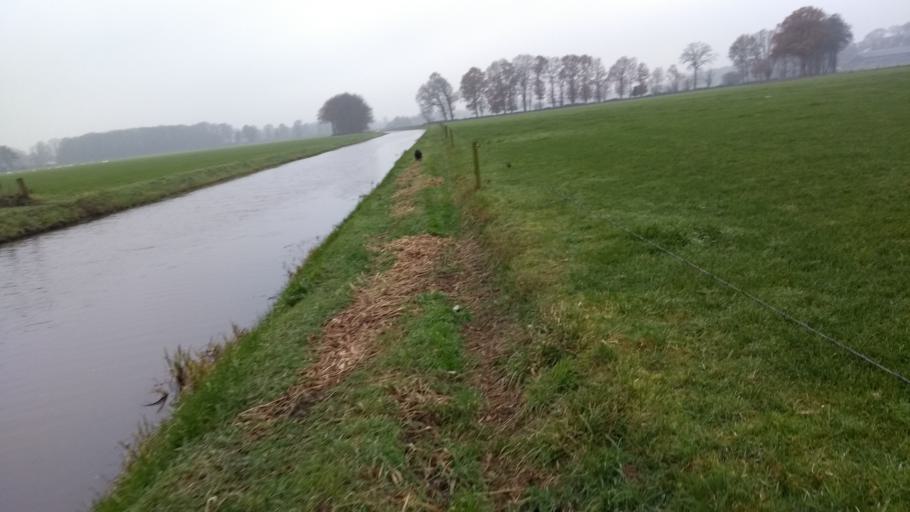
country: NL
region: Overijssel
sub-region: Gemeente Borne
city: Borne
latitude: 52.3432
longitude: 6.7416
